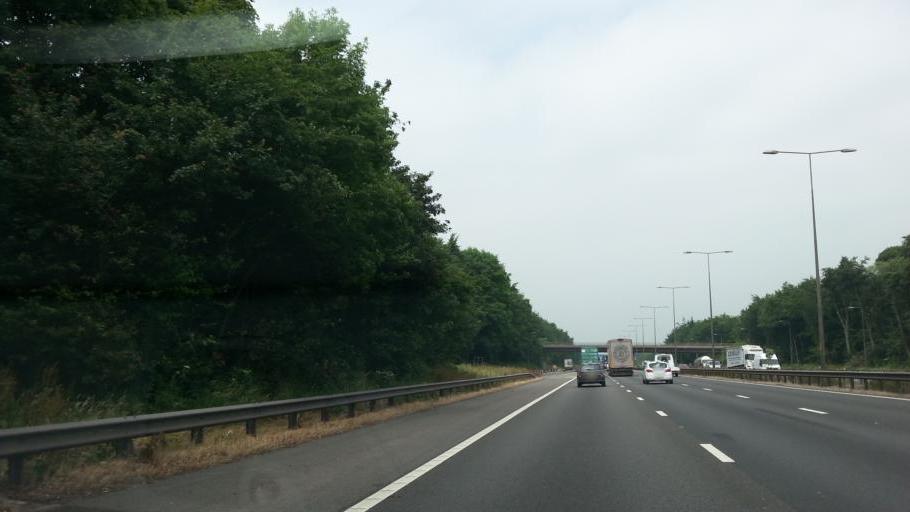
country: GB
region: England
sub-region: Staffordshire
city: Essington
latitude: 52.6450
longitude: -2.0575
